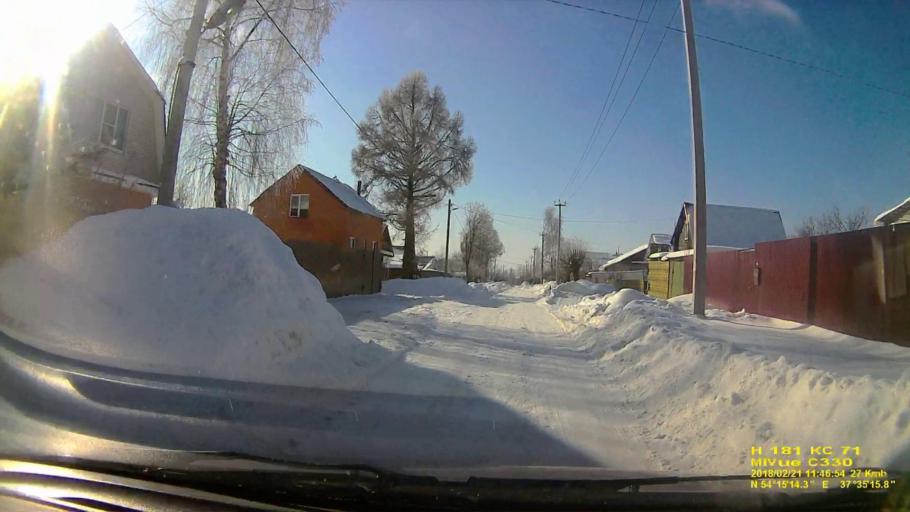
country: RU
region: Tula
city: Gorelki
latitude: 54.2539
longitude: 37.5877
